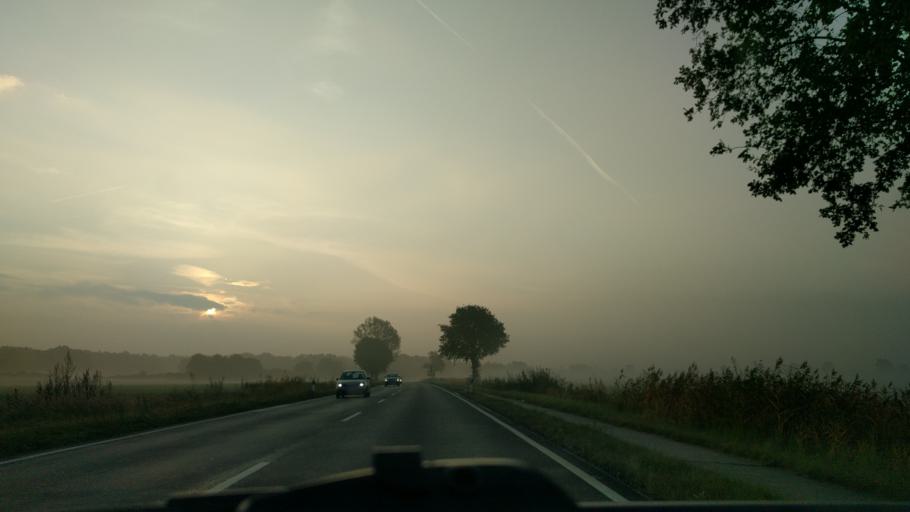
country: DE
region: Lower Saxony
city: Isenbuttel
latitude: 52.4427
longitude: 10.5970
